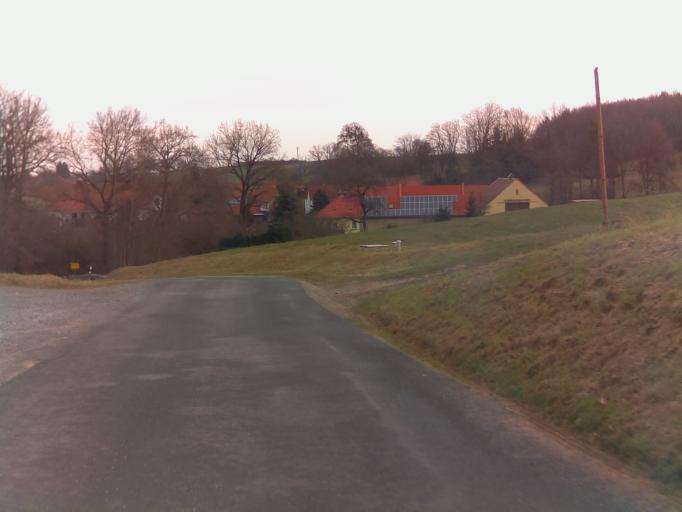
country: DE
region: Thuringia
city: Hundhaupten
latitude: 50.8265
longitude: 11.9838
